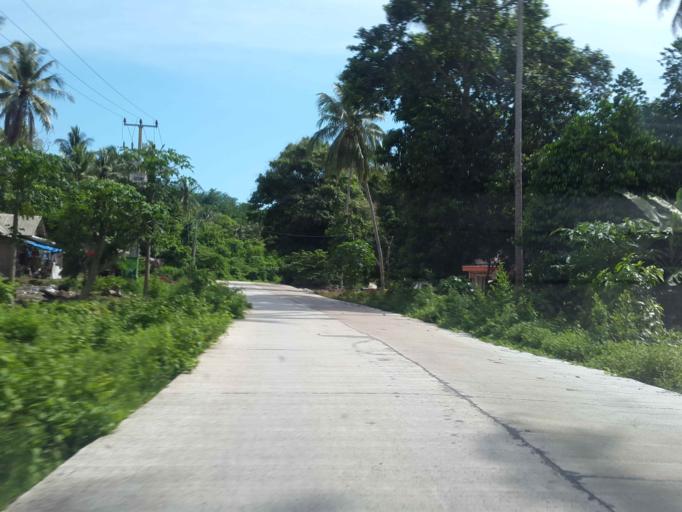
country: ID
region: Banten
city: Babakanbungur
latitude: -6.5318
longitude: 105.6254
